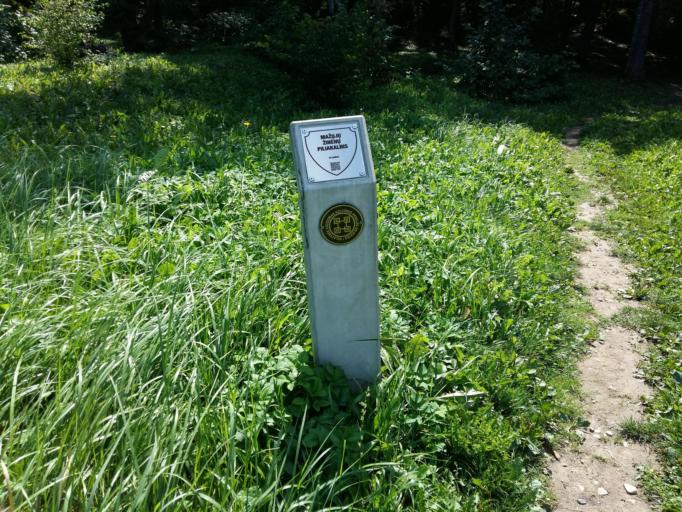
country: LT
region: Kauno apskritis
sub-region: Kauno rajonas
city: Karmelava
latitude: 55.0330
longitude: 24.1124
